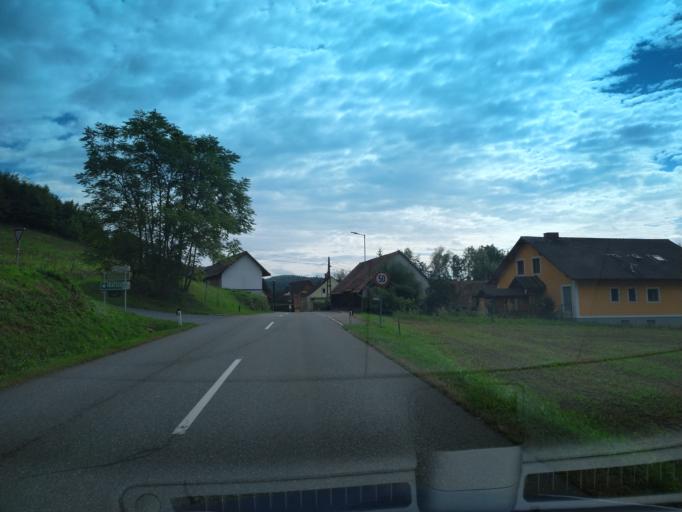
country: AT
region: Styria
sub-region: Politischer Bezirk Leibnitz
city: Heimschuh
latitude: 46.7781
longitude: 15.4998
